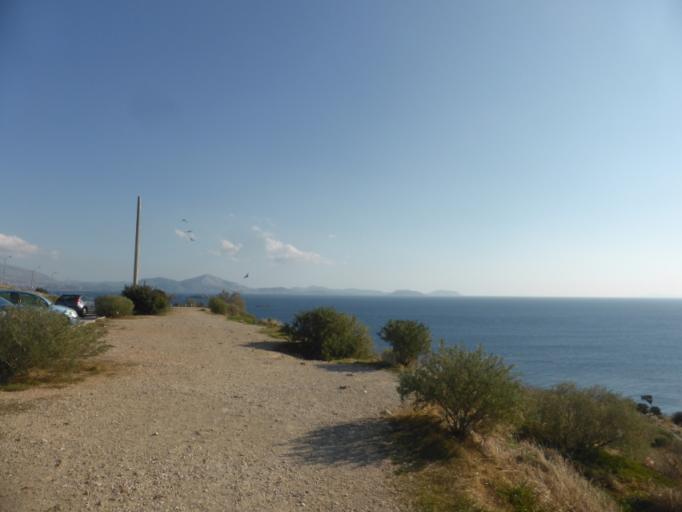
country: GR
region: Attica
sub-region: Nomarchia Anatolikis Attikis
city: Vouliagmeni
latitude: 37.8021
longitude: 23.7931
